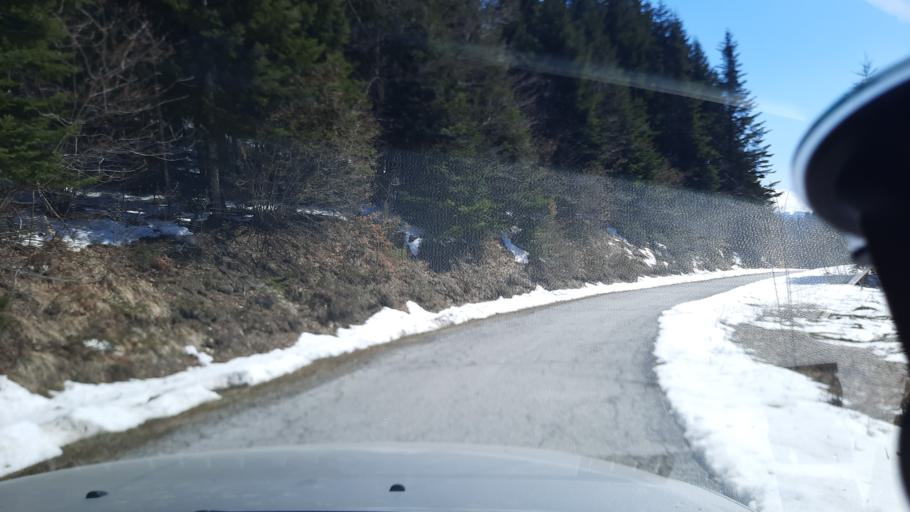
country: MK
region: Gostivar
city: Vrutok
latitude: 41.7038
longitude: 20.7419
